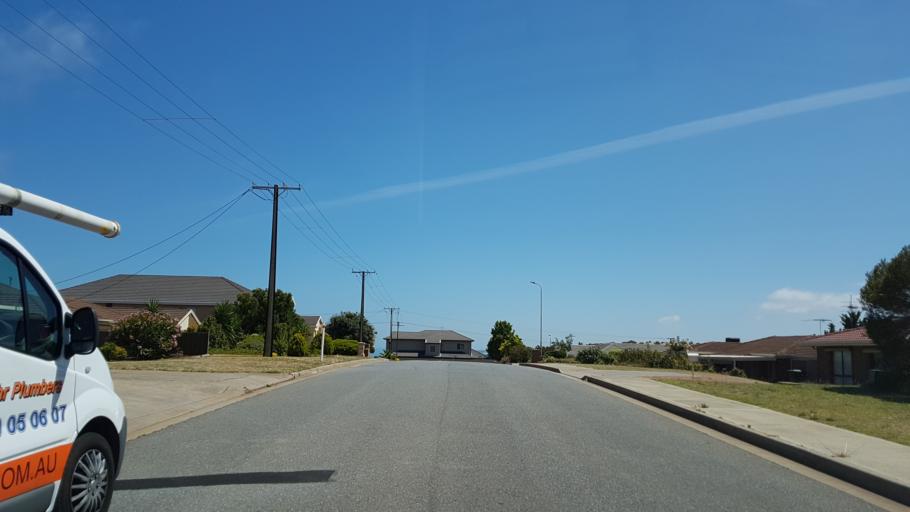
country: AU
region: South Australia
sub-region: Marion
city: Marino
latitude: -35.0639
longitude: 138.5088
